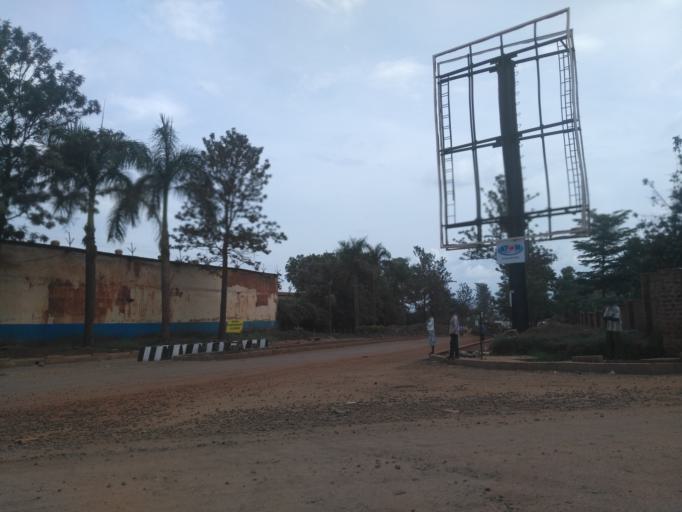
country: UG
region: Eastern Region
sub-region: Jinja District
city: Jinja
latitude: 0.4356
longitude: 33.2132
